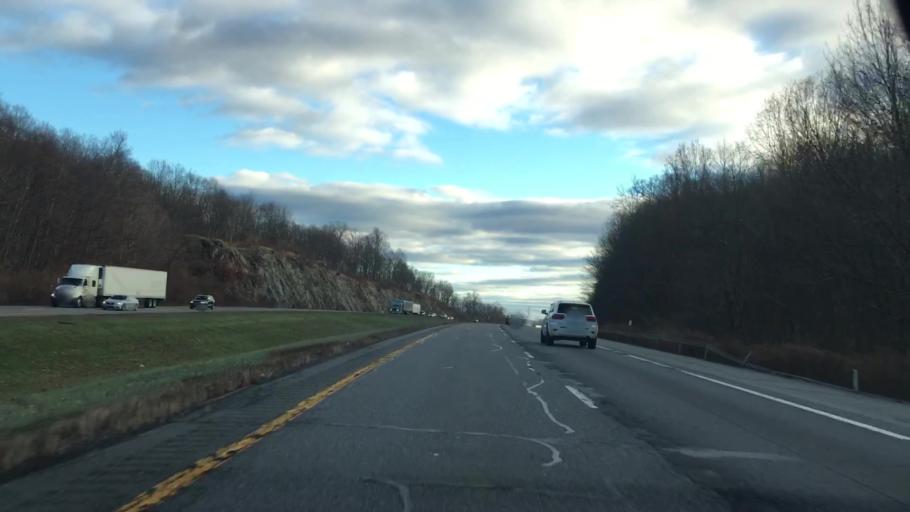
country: US
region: New York
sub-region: Putnam County
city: Brewster Hill
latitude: 41.4420
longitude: -73.6331
